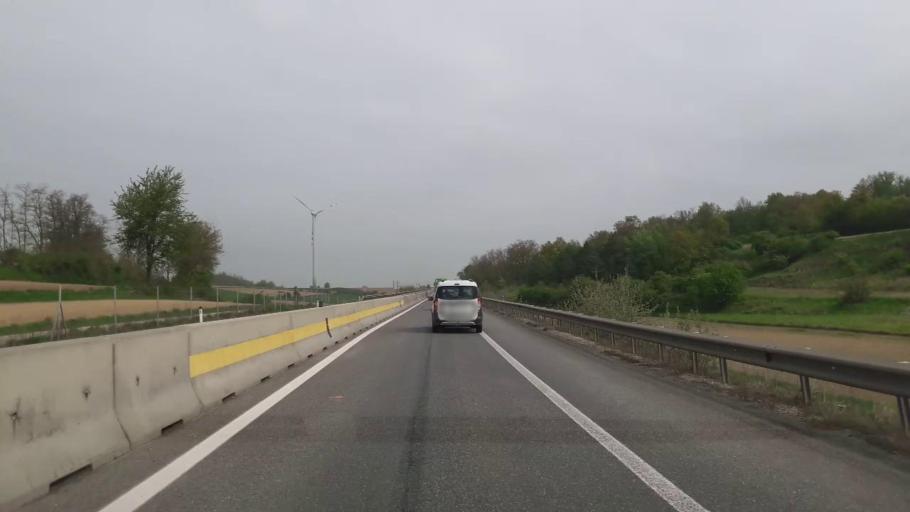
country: AT
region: Lower Austria
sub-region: Politischer Bezirk Hollabrunn
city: Hollabrunn
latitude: 48.5226
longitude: 16.0843
